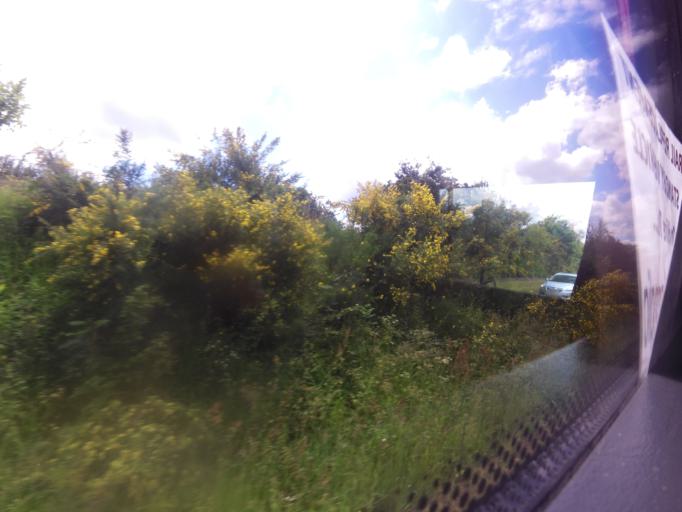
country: GB
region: England
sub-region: Norfolk
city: Cromer
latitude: 52.9242
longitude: 1.2831
